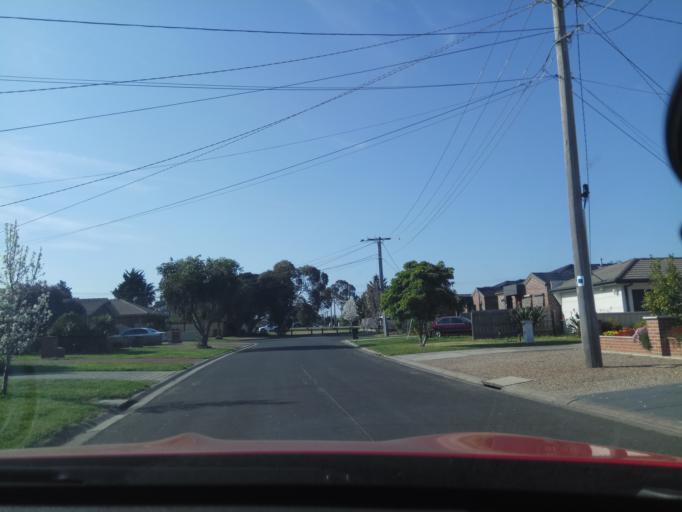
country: AU
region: Victoria
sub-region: Hobsons Bay
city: Laverton
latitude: -37.8723
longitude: 144.7740
